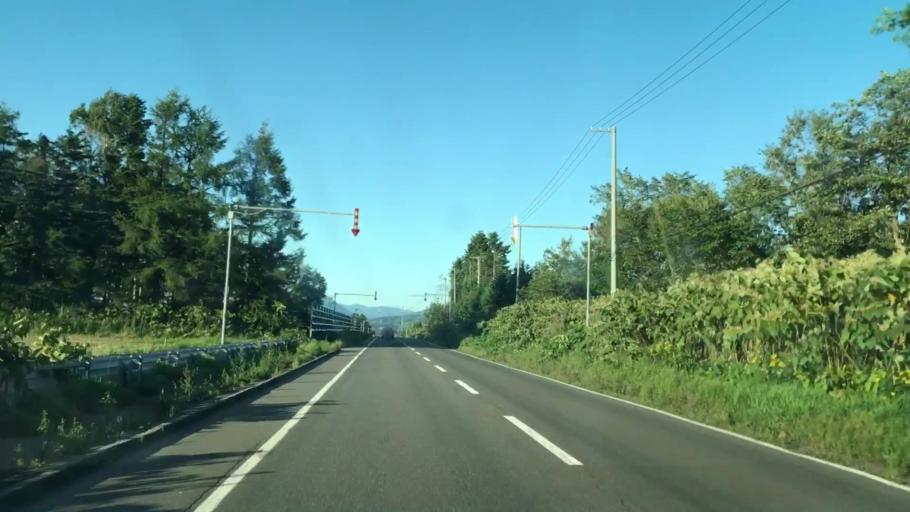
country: JP
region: Hokkaido
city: Date
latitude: 42.6191
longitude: 140.7921
